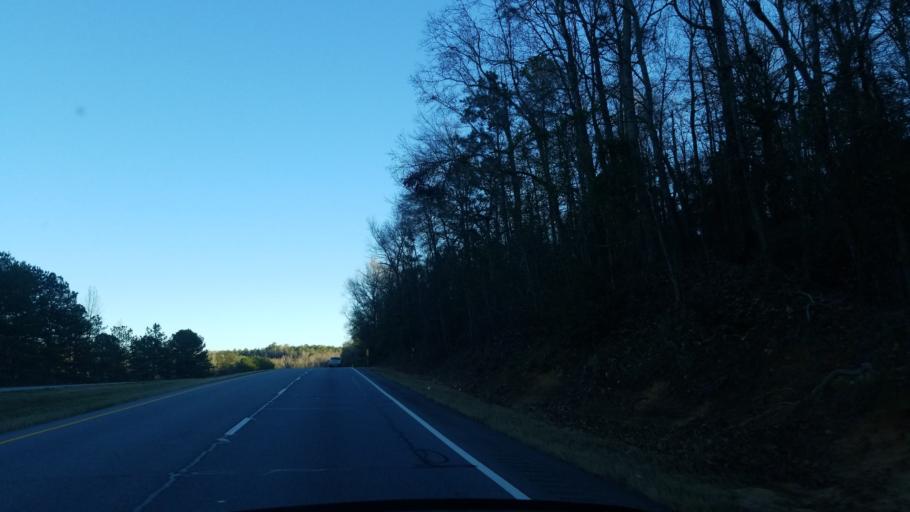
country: US
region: Georgia
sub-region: Chattahoochee County
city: Cusseta
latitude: 32.2623
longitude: -84.7334
